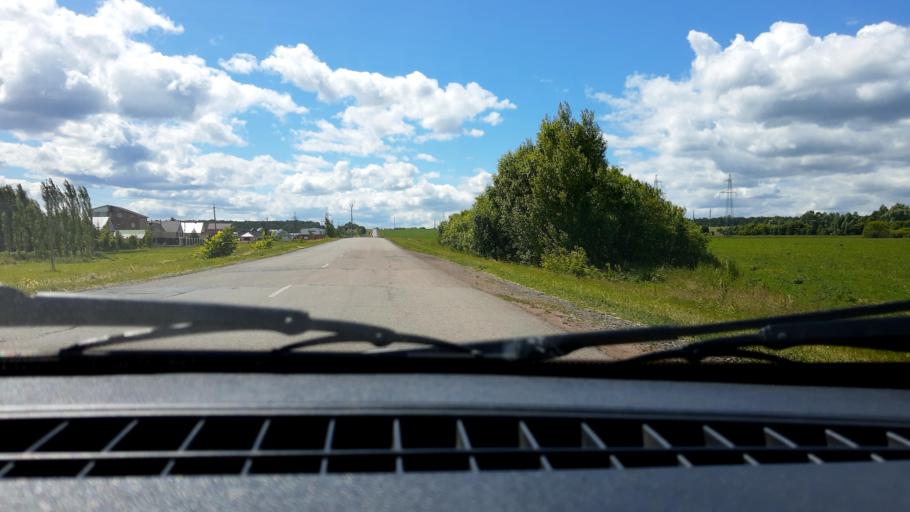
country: RU
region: Bashkortostan
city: Mikhaylovka
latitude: 54.8315
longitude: 55.9151
